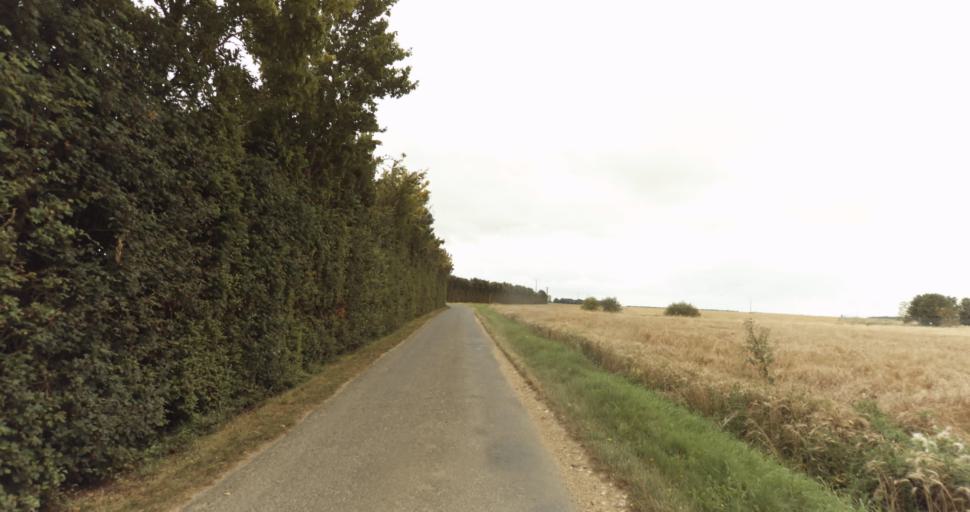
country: FR
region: Haute-Normandie
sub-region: Departement de l'Eure
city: Gravigny
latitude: 49.0355
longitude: 1.2147
